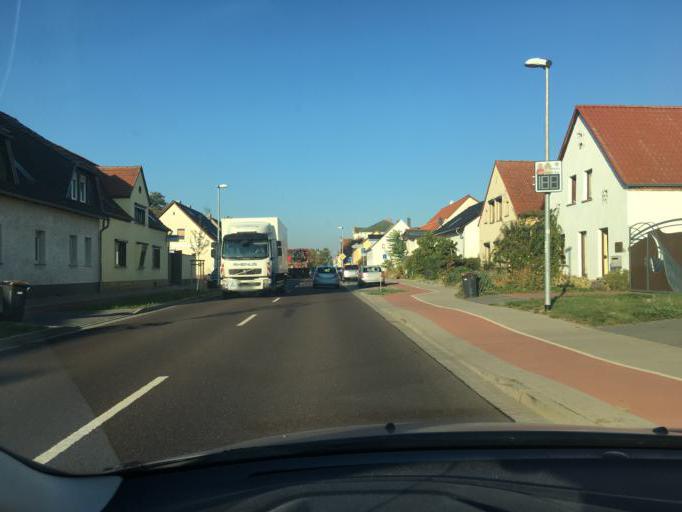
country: DE
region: Saxony-Anhalt
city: Borne
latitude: 51.9980
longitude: 11.5400
